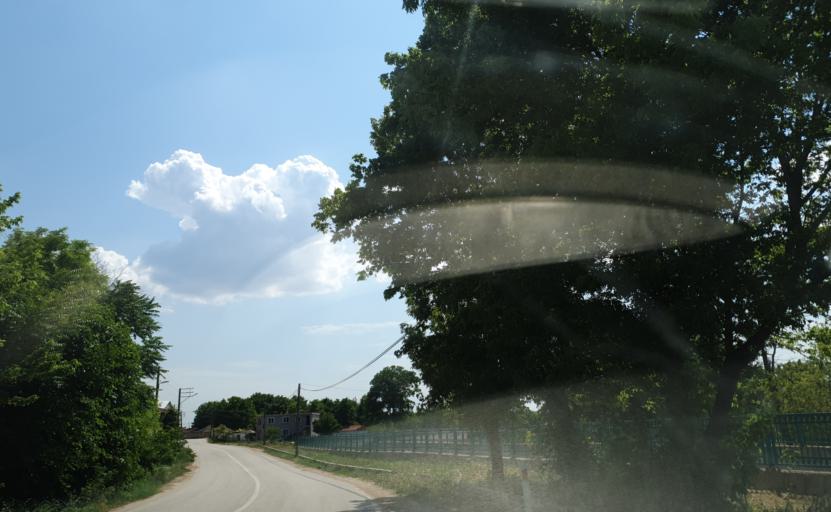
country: TR
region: Tekirdag
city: Beyazkoy
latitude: 41.4581
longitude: 27.6454
